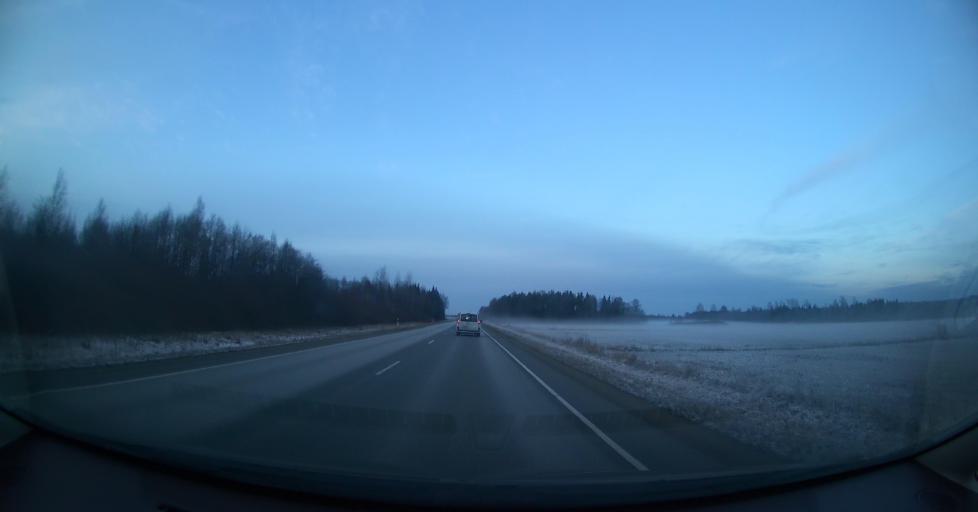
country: EE
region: Jogevamaa
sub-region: Poltsamaa linn
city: Poltsamaa
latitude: 58.7557
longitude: 25.7624
